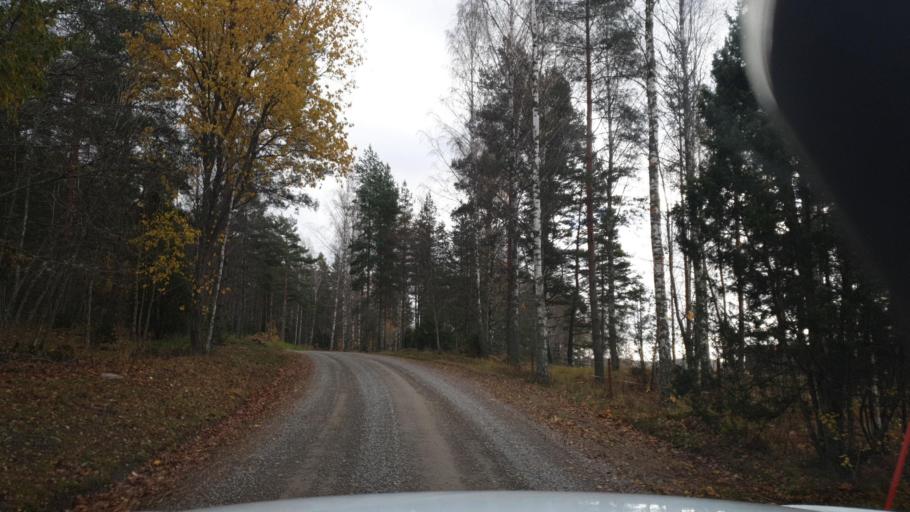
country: SE
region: Vaermland
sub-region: Arvika Kommun
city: Arvika
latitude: 59.4970
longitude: 12.7297
